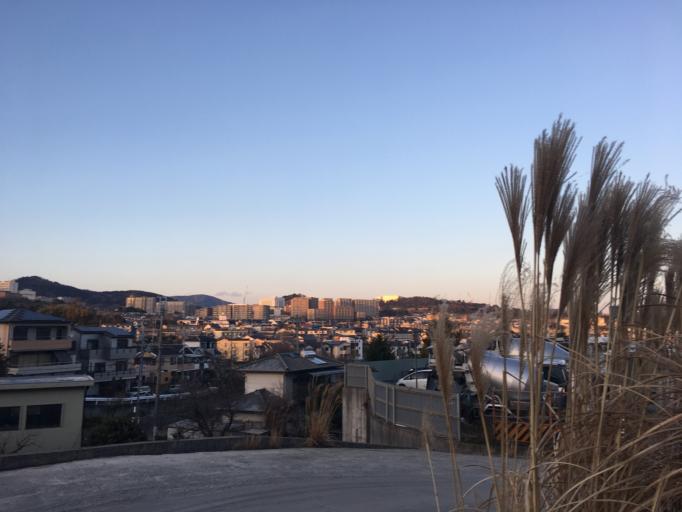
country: JP
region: Osaka
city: Mino
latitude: 34.8434
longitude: 135.5156
